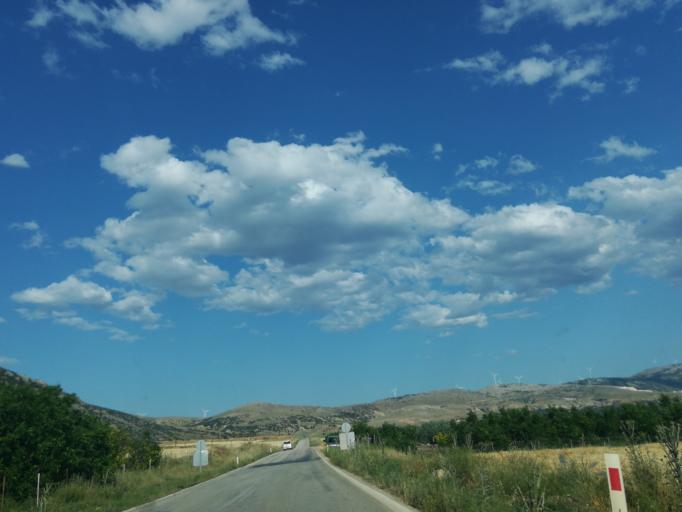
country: TR
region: Afyonkarahisar
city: Dinar
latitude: 38.1006
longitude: 30.1347
